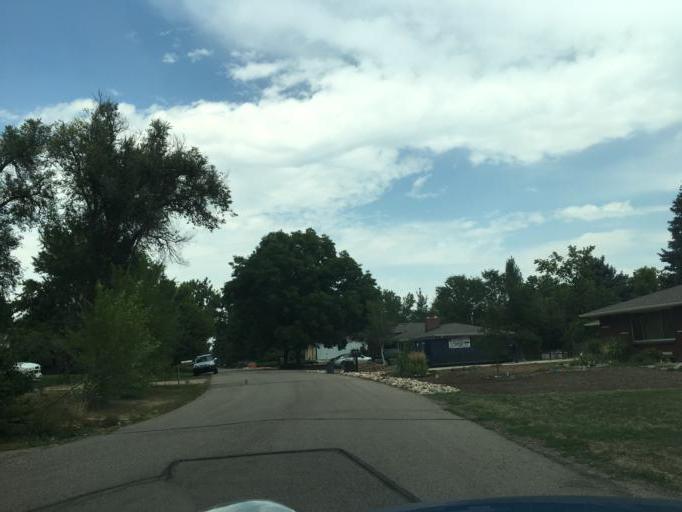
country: US
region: Colorado
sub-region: Jefferson County
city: Wheat Ridge
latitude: 39.7446
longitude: -105.0945
